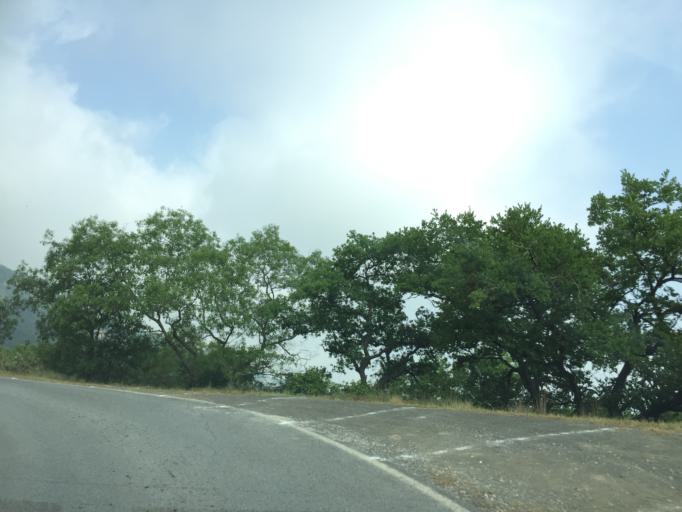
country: MX
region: Nuevo Leon
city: Garza Garcia
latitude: 25.6195
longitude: -100.3622
